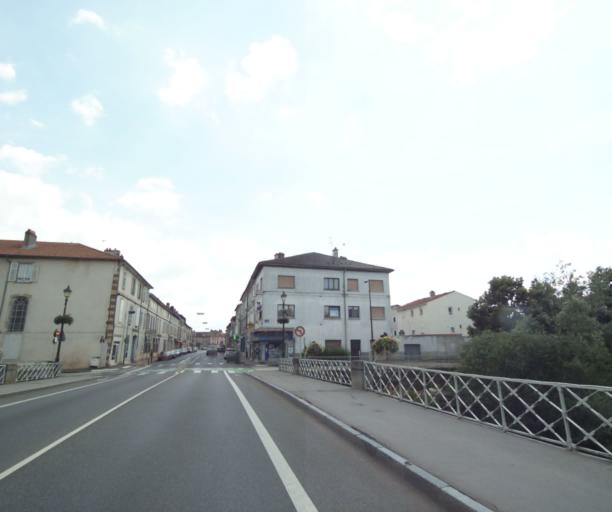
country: FR
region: Lorraine
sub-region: Departement de Meurthe-et-Moselle
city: Luneville
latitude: 48.5973
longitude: 6.4892
